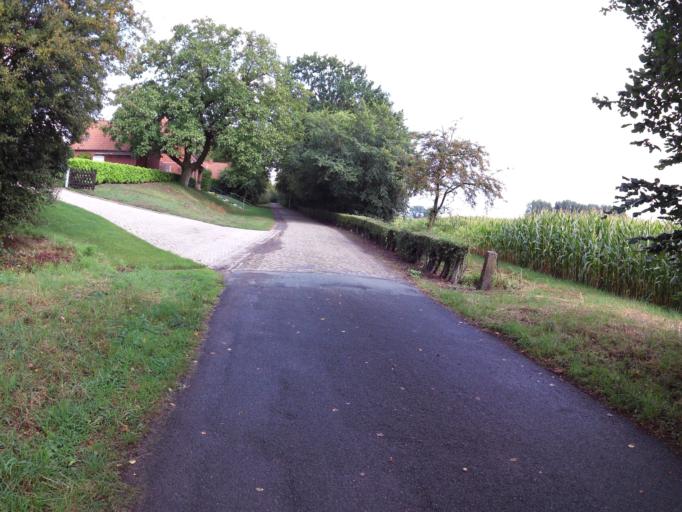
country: DE
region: Lower Saxony
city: Balge
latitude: 52.7211
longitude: 9.1943
